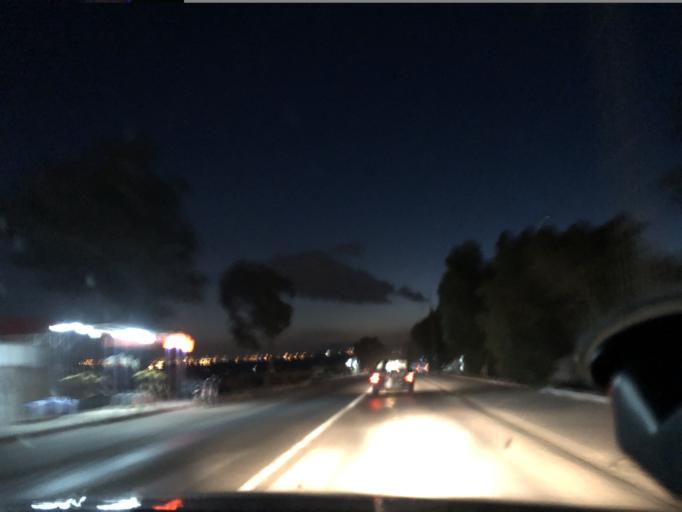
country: TN
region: Al Qasrayn
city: Kasserine
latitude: 35.2091
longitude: 8.8938
